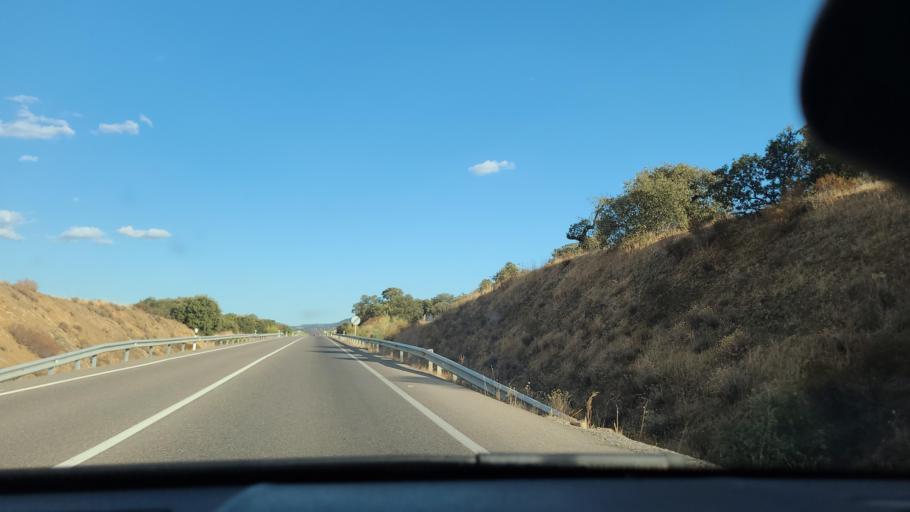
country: ES
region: Andalusia
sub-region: Province of Cordoba
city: Belmez
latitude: 38.2268
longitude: -5.1620
